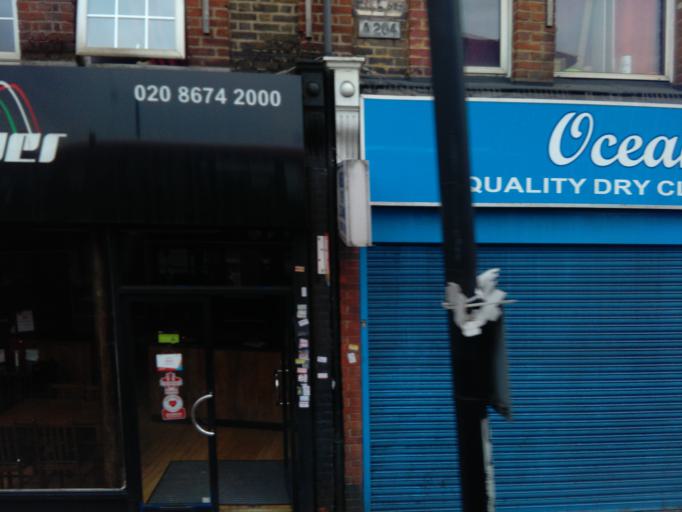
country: GB
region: England
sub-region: Greater London
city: Brixton Hill
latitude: 51.4410
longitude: -0.1068
